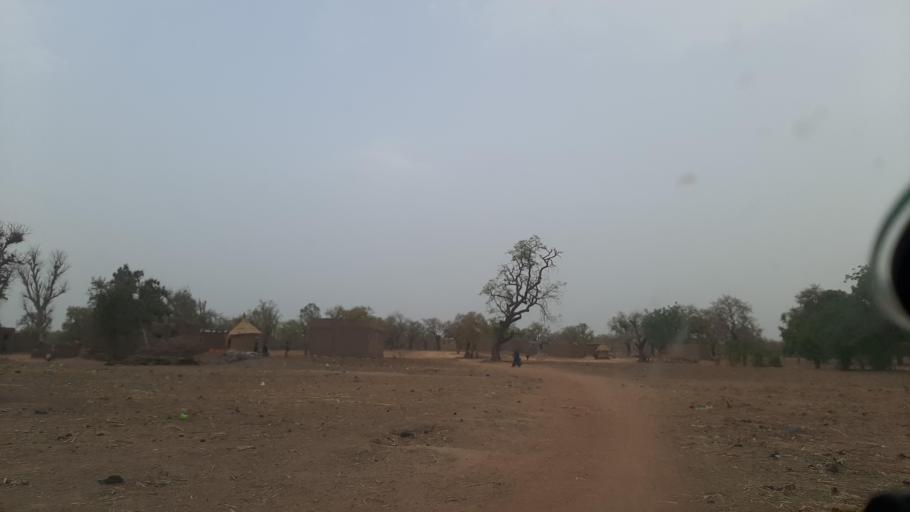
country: BF
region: Boucle du Mouhoun
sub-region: Province des Banwa
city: Salanso
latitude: 11.8696
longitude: -4.4486
